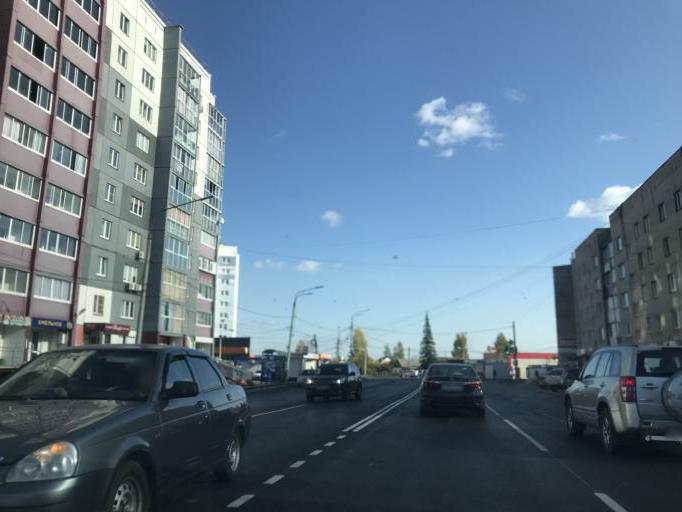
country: RU
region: Chelyabinsk
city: Roshchino
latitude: 55.2350
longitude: 61.2992
